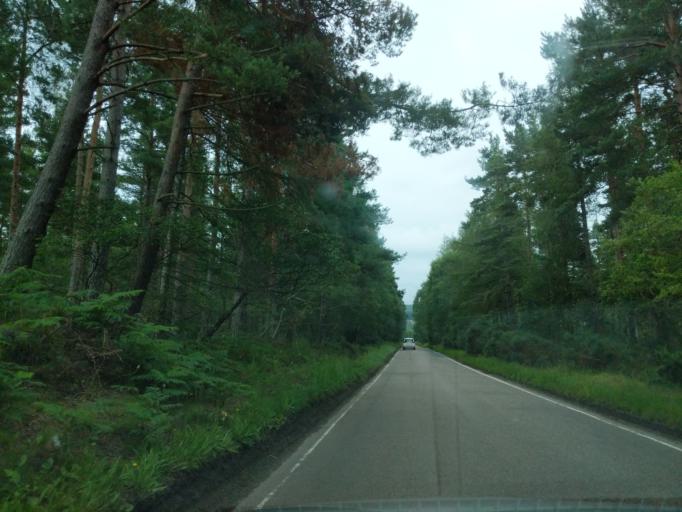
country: GB
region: Scotland
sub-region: Moray
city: Kinloss
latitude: 57.5727
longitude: -3.5360
